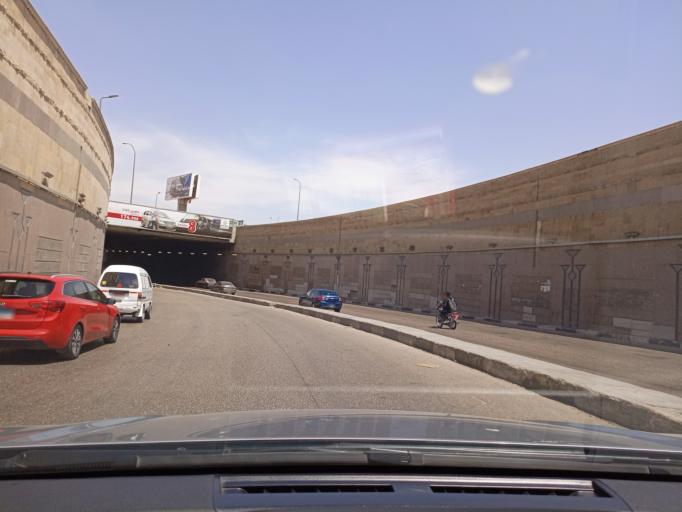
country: EG
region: Muhafazat al Qalyubiyah
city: Al Khankah
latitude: 30.1627
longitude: 31.4786
